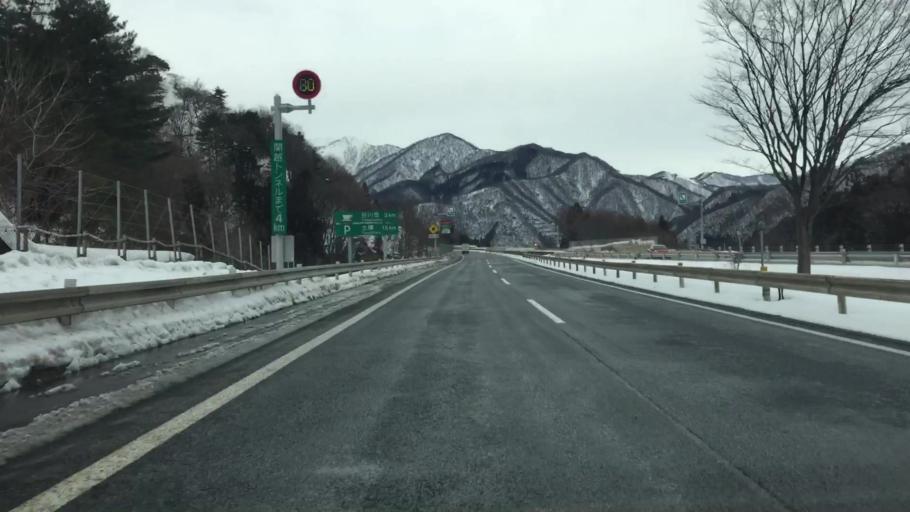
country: JP
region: Gunma
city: Numata
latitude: 36.7581
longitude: 138.9660
